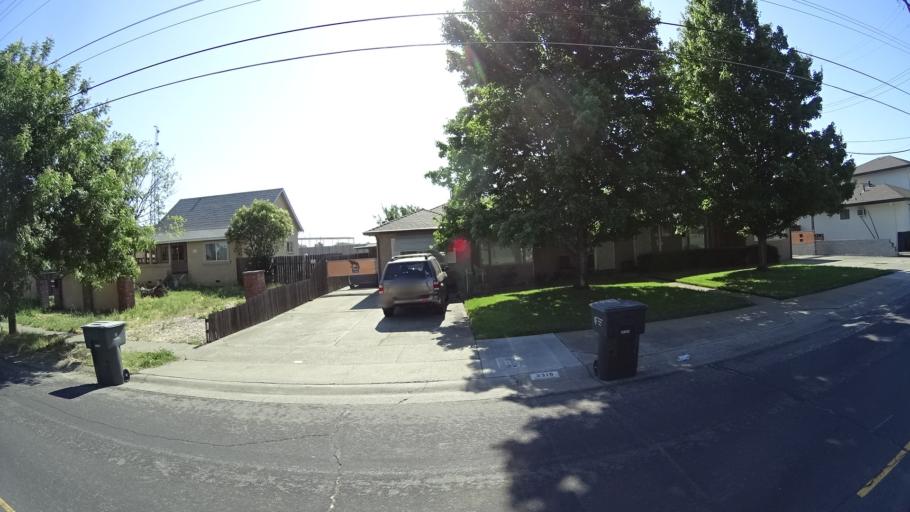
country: US
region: California
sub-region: Sacramento County
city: Florin
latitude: 38.5435
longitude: -121.4232
